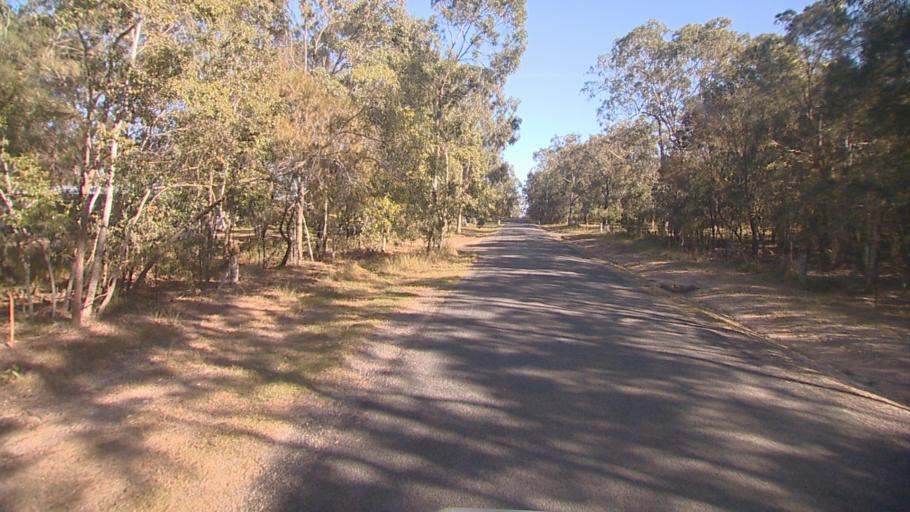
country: AU
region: Queensland
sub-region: Ipswich
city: Springfield Lakes
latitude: -27.6905
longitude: 152.9337
